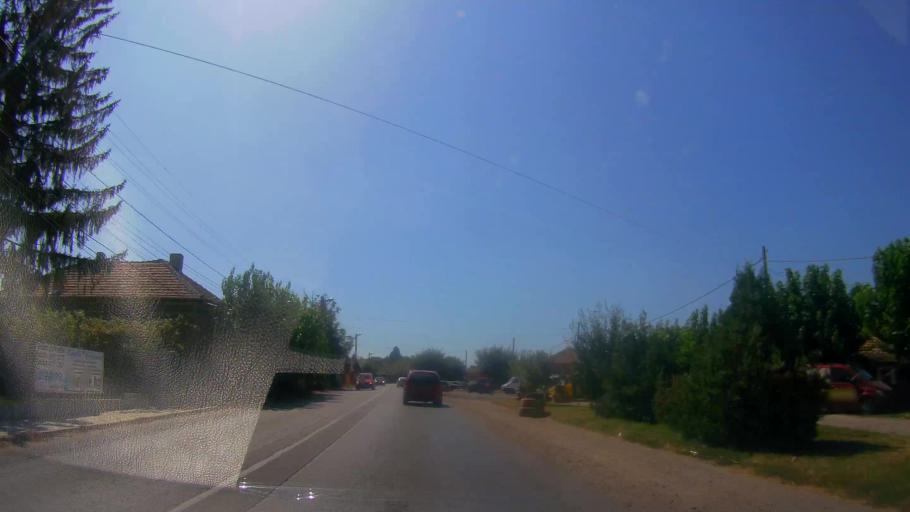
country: BG
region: Veliko Turnovo
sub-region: Obshtina Gorna Oryakhovitsa
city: Purvomaytsi
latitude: 43.1837
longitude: 25.6200
